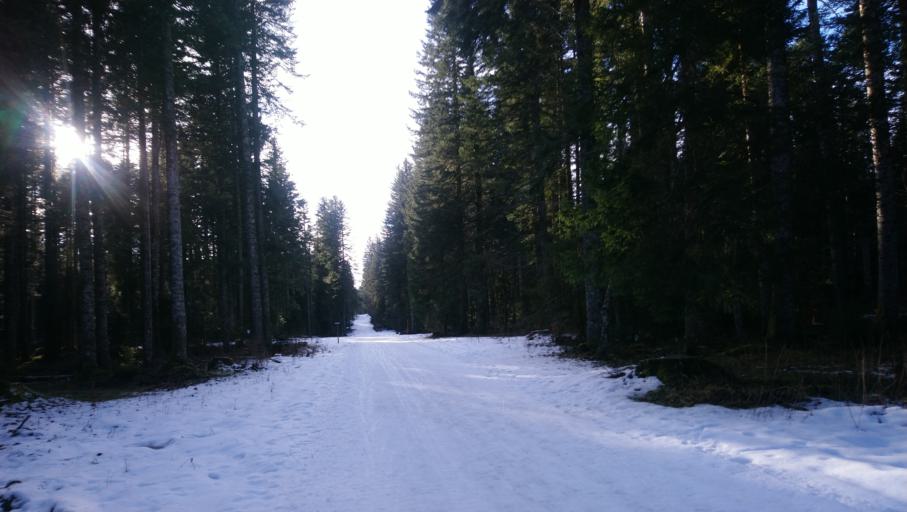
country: FR
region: Franche-Comte
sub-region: Departement du Doubs
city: Les Fourgs
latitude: 46.8269
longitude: 6.4273
